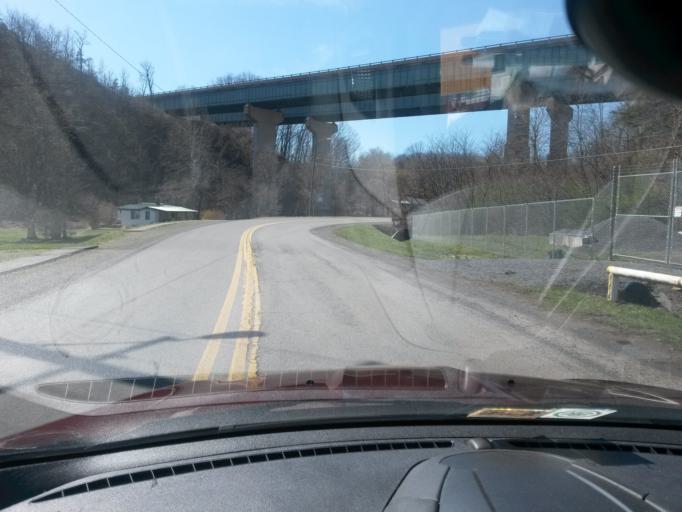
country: US
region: West Virginia
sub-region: Greenbrier County
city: White Sulphur Springs
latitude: 37.7916
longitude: -80.2918
